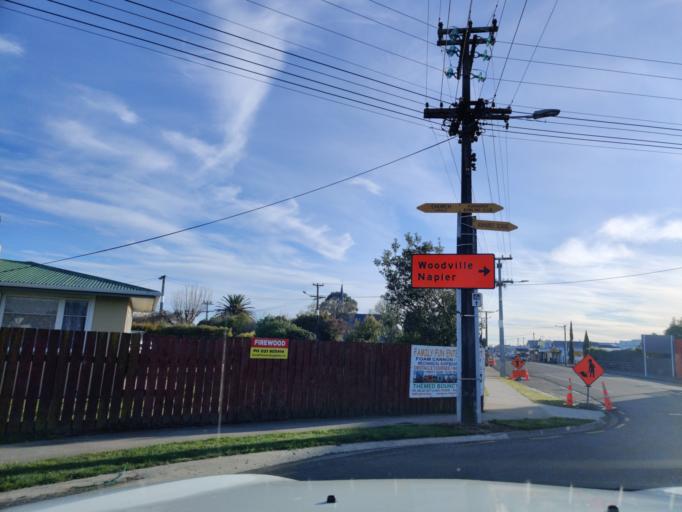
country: NZ
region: Manawatu-Wanganui
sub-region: Palmerston North City
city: Palmerston North
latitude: -40.2928
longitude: 175.7540
